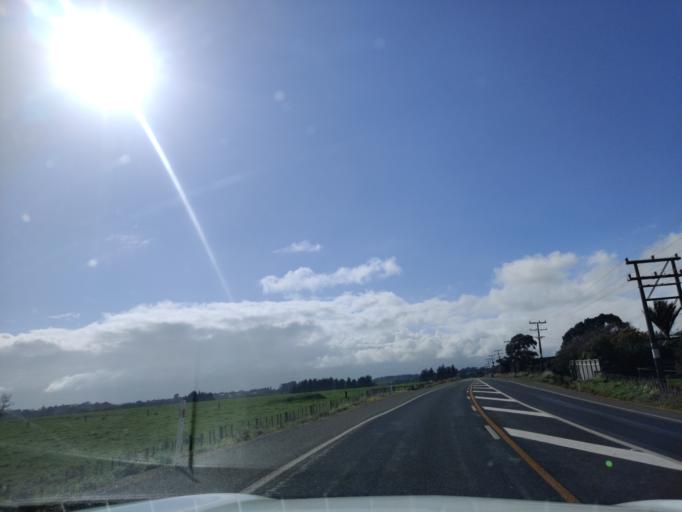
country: NZ
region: Manawatu-Wanganui
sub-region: Palmerston North City
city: Palmerston North
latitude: -40.3996
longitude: 175.6216
